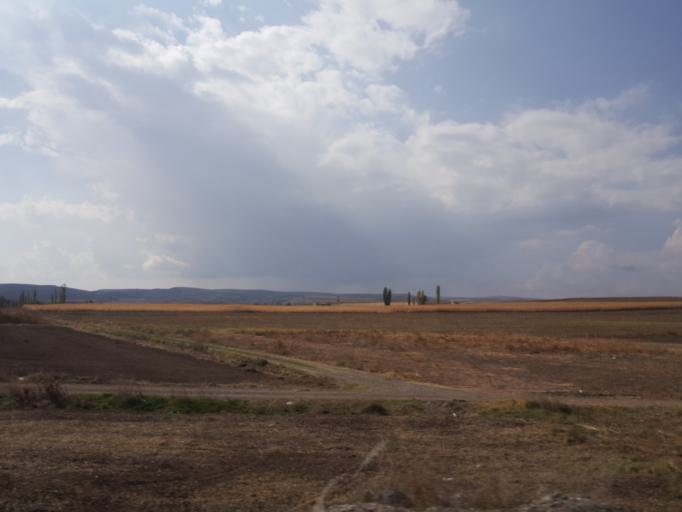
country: TR
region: Corum
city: Alaca
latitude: 40.1466
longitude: 34.8877
